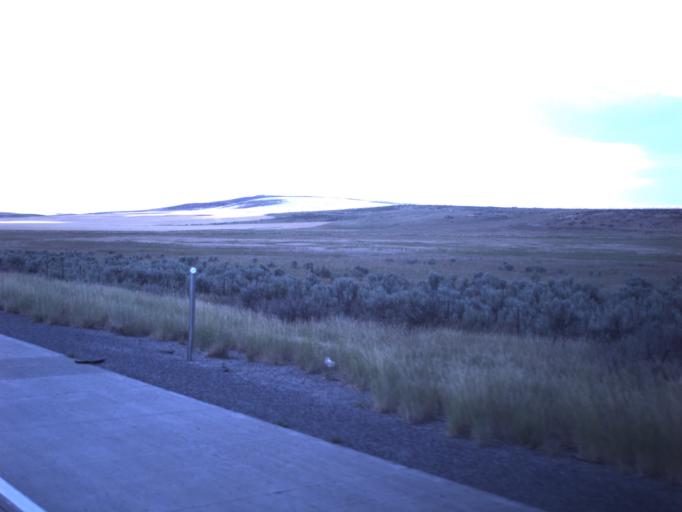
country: US
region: Utah
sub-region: Box Elder County
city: Garland
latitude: 41.8788
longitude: -112.4752
